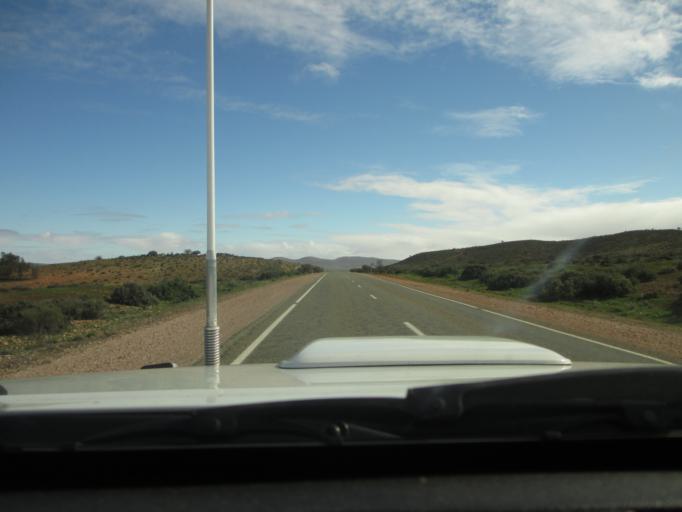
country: AU
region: South Australia
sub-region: Flinders Ranges
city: Quorn
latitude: -31.7845
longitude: 138.3496
